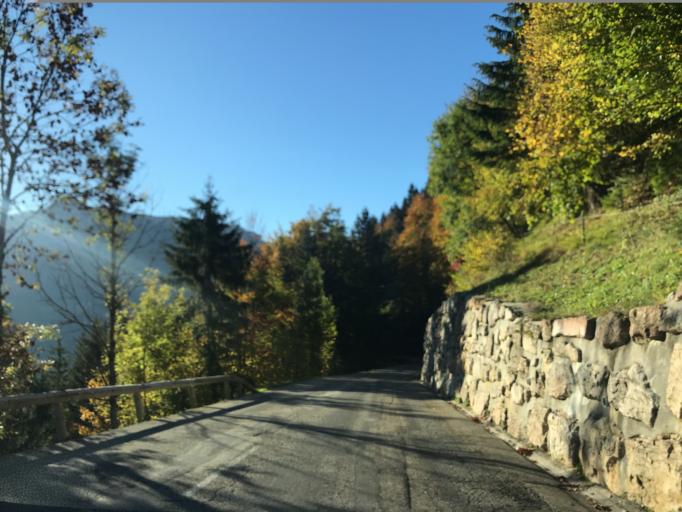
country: FR
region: Rhone-Alpes
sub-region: Departement de la Savoie
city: Vimines
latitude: 45.4573
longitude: 5.8658
